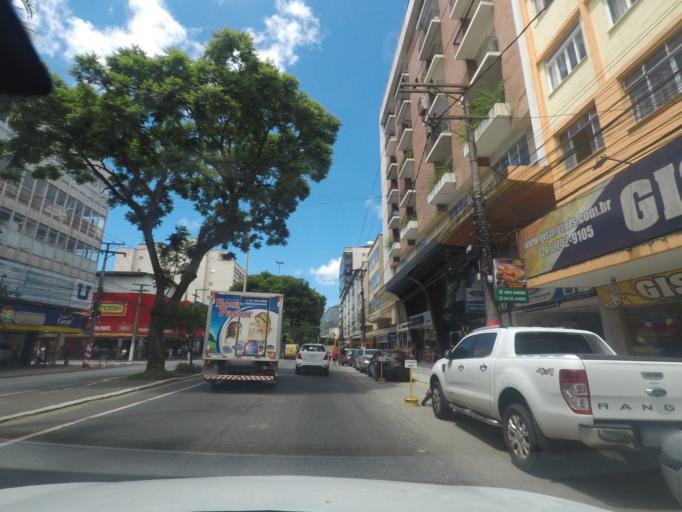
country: BR
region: Rio de Janeiro
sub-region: Teresopolis
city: Teresopolis
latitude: -22.4140
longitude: -42.9704
